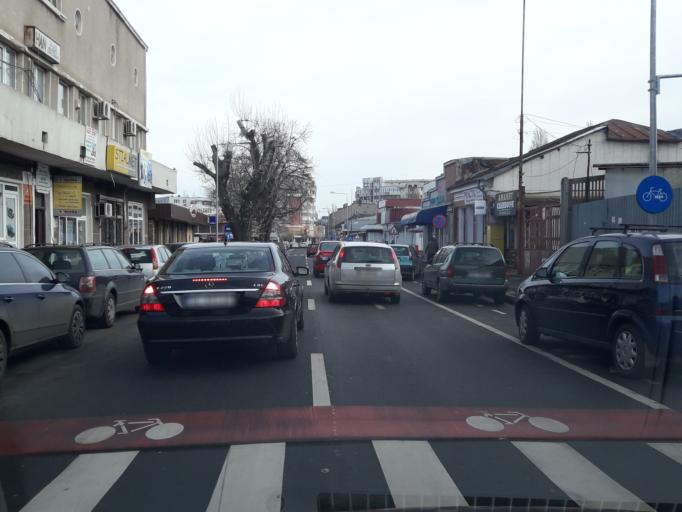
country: RO
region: Galati
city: Galati
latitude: 45.4376
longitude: 28.0470
